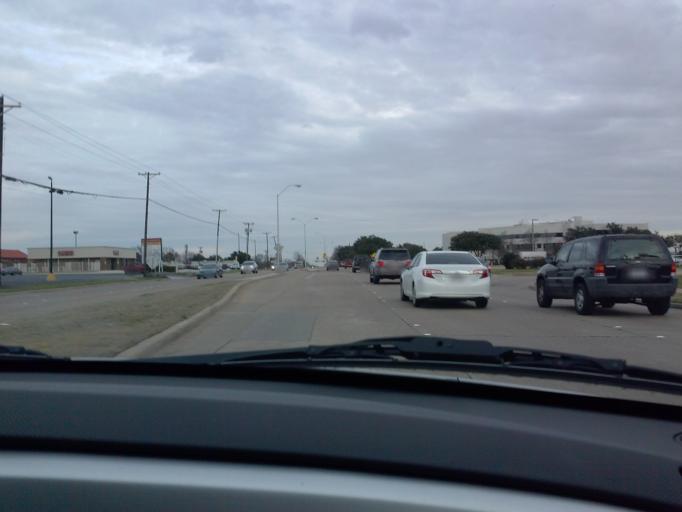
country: US
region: Texas
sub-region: Collin County
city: Plano
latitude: 33.0193
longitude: -96.7490
